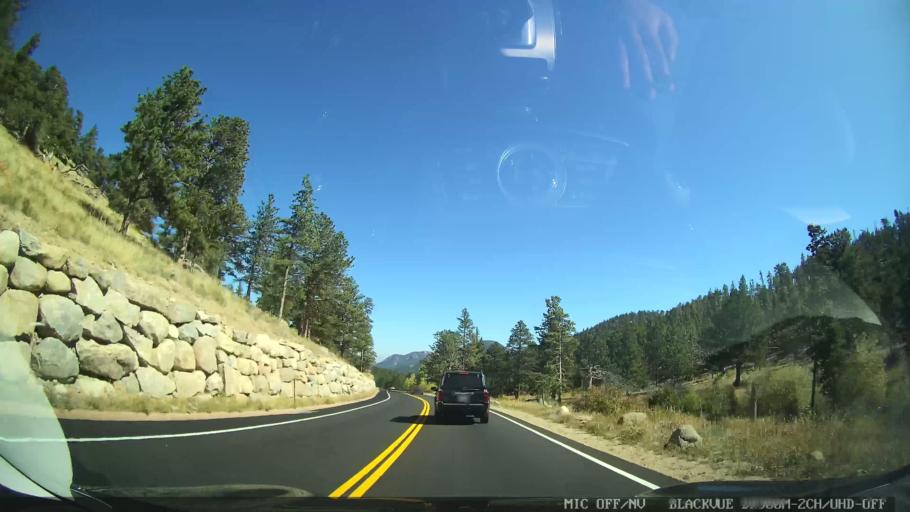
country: US
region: Colorado
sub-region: Larimer County
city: Estes Park
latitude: 40.3428
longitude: -105.5988
